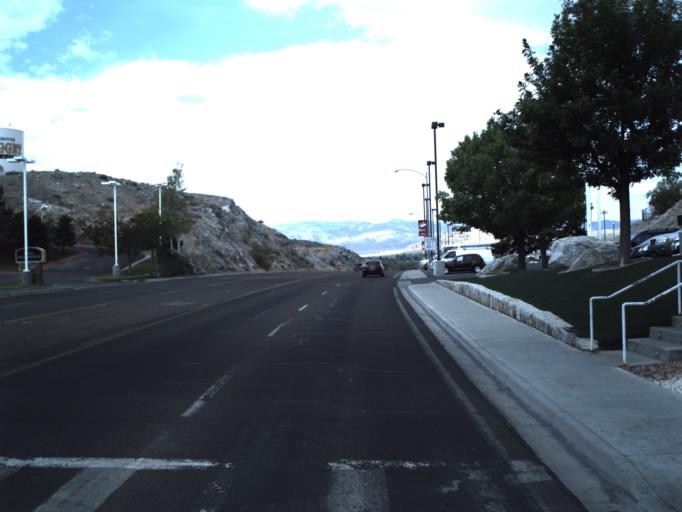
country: US
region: Utah
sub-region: Tooele County
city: Wendover
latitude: 40.7358
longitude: -114.0446
